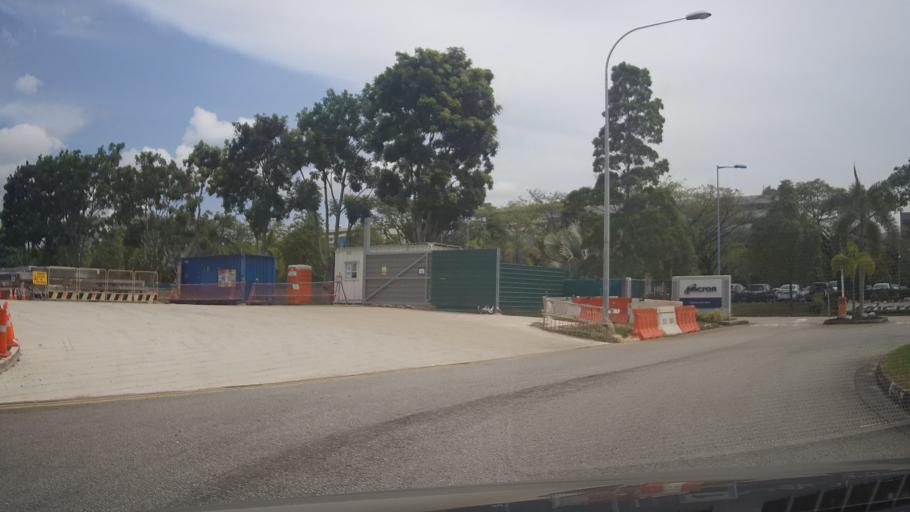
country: MY
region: Johor
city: Johor Bahru
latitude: 1.4560
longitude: 103.7952
